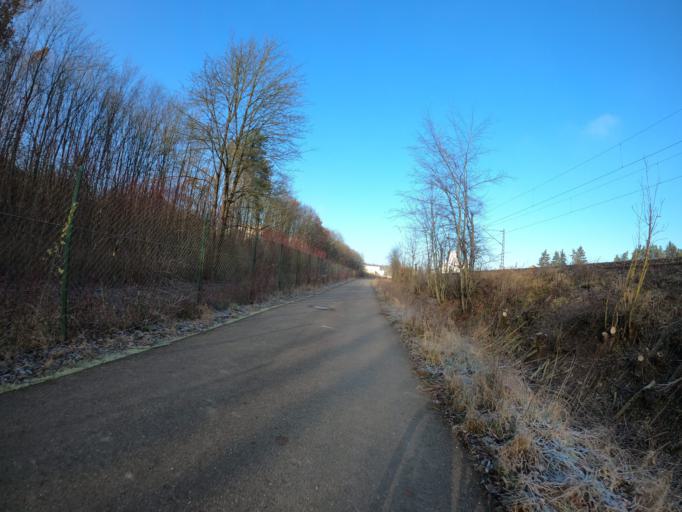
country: DE
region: Baden-Wuerttemberg
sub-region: Tuebingen Region
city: Amstetten
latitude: 48.5667
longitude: 9.8798
